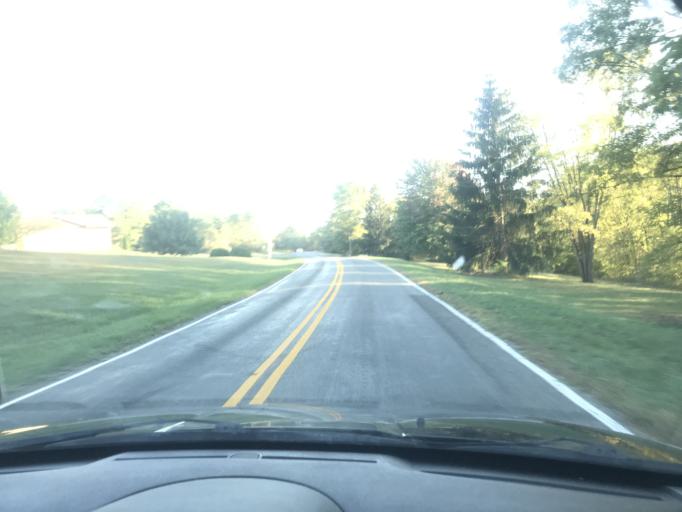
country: US
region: Ohio
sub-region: Logan County
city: De Graff
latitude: 40.2485
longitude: -83.8662
